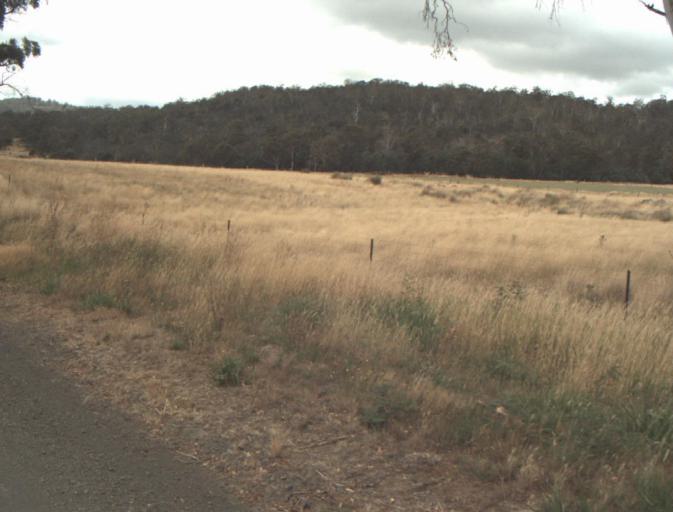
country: AU
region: Tasmania
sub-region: Northern Midlands
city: Evandale
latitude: -41.5263
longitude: 147.3614
